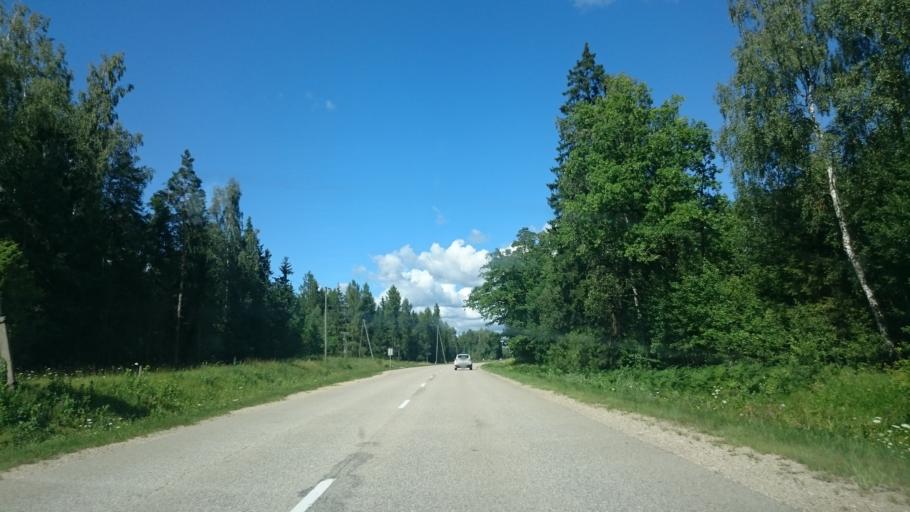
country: LV
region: Kuldigas Rajons
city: Kuldiga
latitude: 56.8849
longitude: 21.8792
